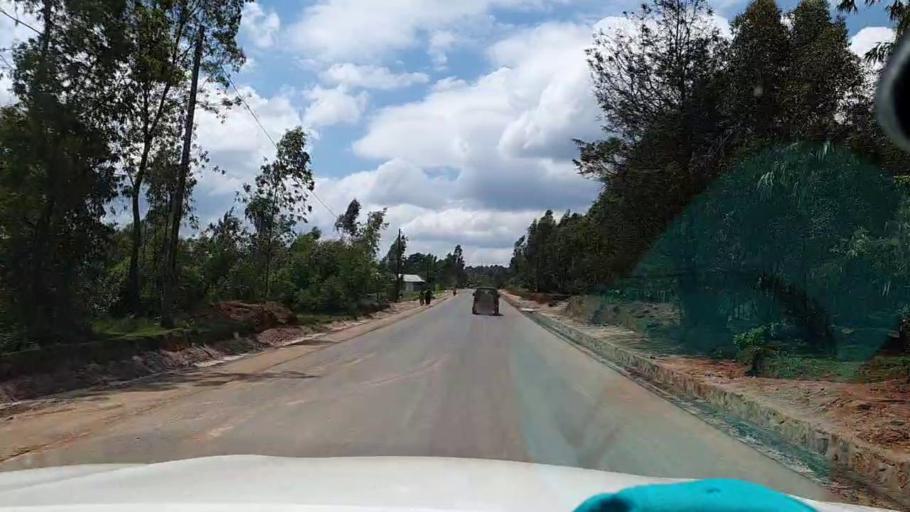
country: RW
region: Southern Province
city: Nzega
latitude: -2.6558
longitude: 29.5602
